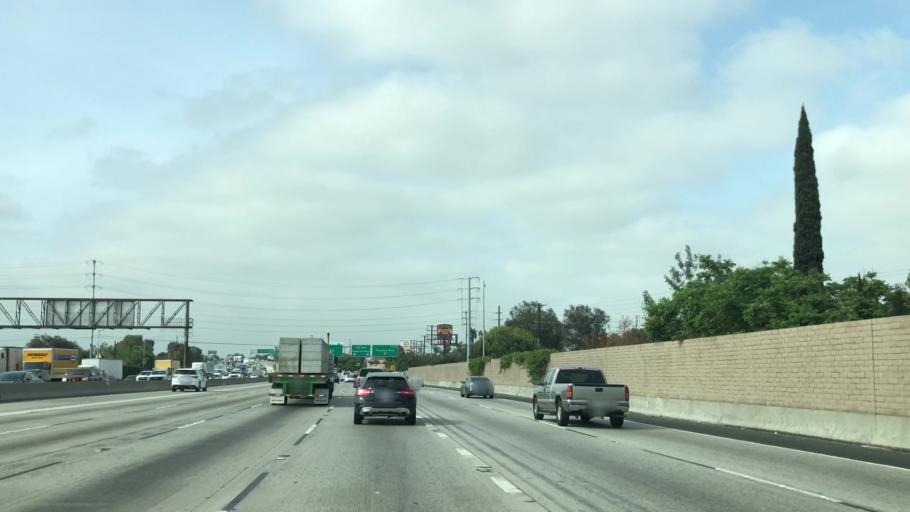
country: US
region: California
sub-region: Los Angeles County
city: Santa Fe Springs
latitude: 33.9298
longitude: -118.1027
